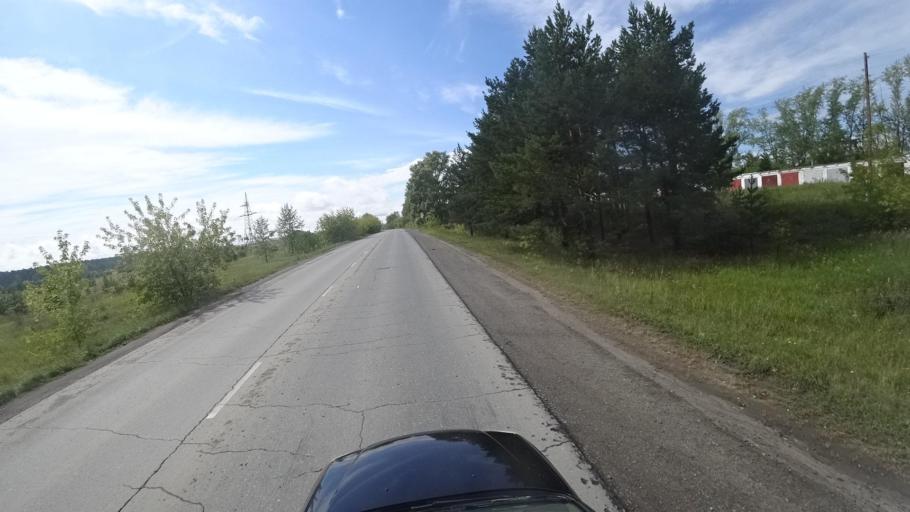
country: RU
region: Sverdlovsk
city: Kamyshlov
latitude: 56.8441
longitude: 62.7714
